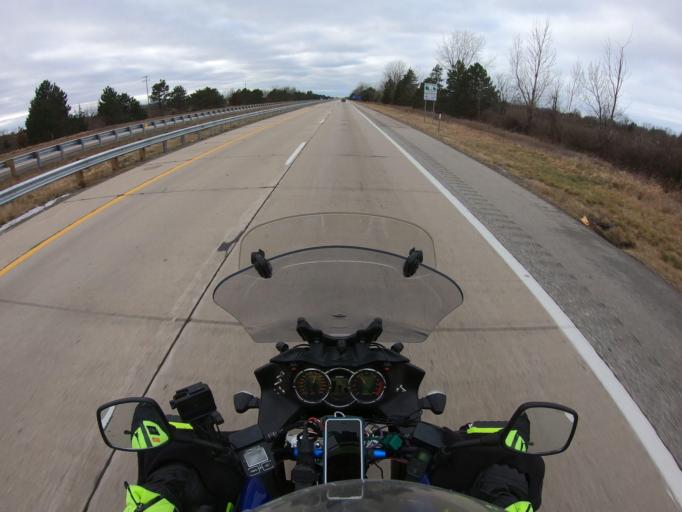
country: US
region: Michigan
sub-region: Bay County
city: Auburn
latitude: 43.5969
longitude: -84.0704
